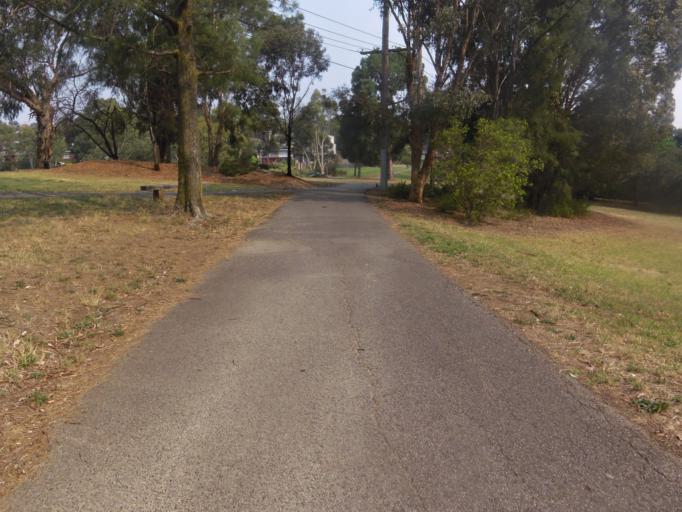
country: AU
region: Victoria
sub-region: Manningham
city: Bulleen
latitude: -37.7713
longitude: 145.0900
